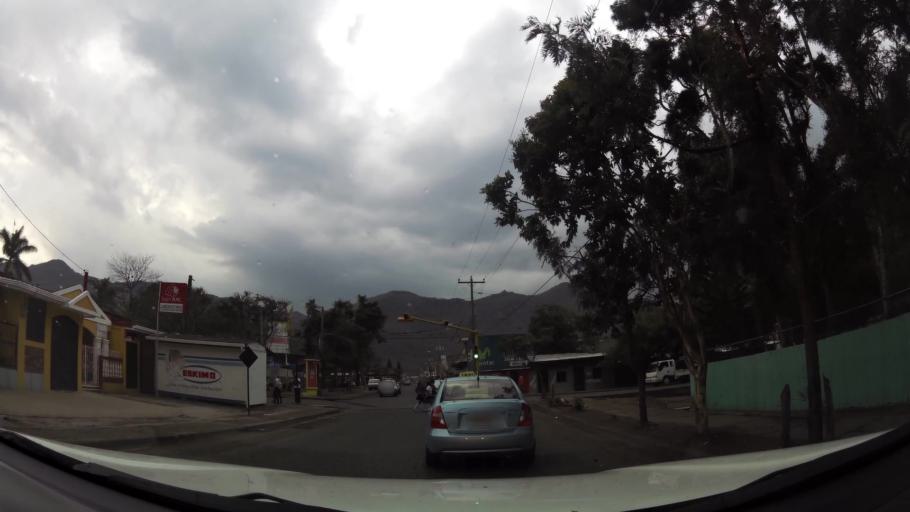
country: NI
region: Jinotega
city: Jinotega
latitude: 13.0887
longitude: -85.9990
